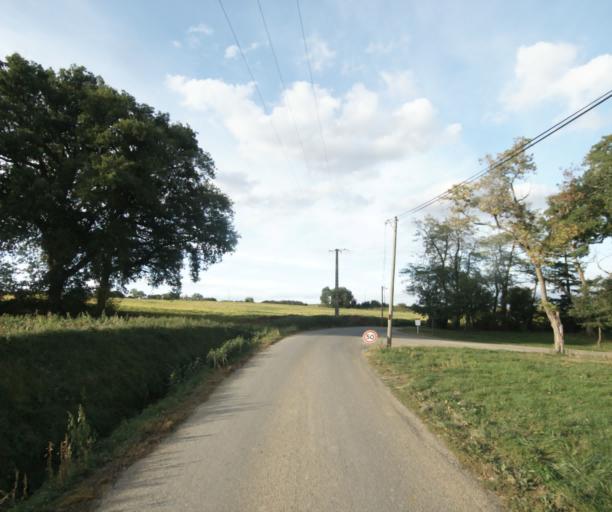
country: FR
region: Midi-Pyrenees
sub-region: Departement du Gers
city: Gondrin
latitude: 43.9056
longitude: 0.2639
